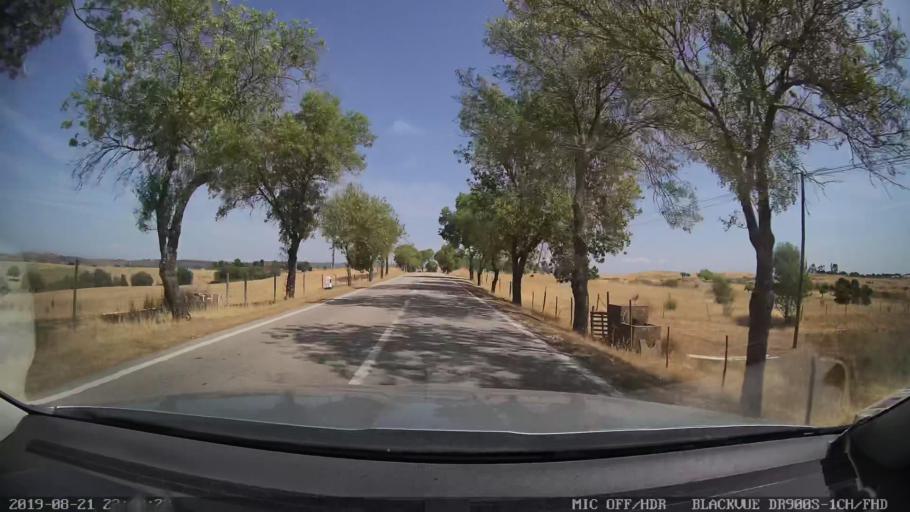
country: PT
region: Castelo Branco
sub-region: Idanha-A-Nova
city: Idanha-a-Nova
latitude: 39.8646
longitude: -7.2576
